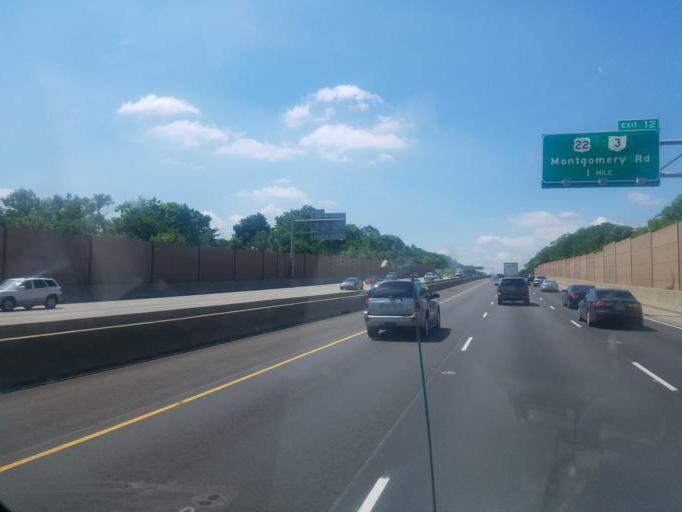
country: US
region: Ohio
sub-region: Hamilton County
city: Kenwood
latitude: 39.2166
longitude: -84.3696
